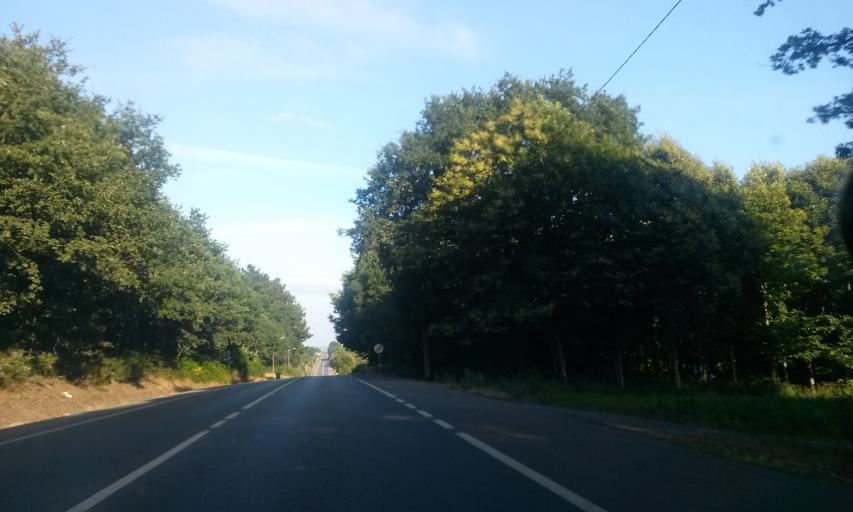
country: ES
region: Galicia
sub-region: Provincia de Lugo
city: Begonte
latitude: 43.1401
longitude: -7.6688
